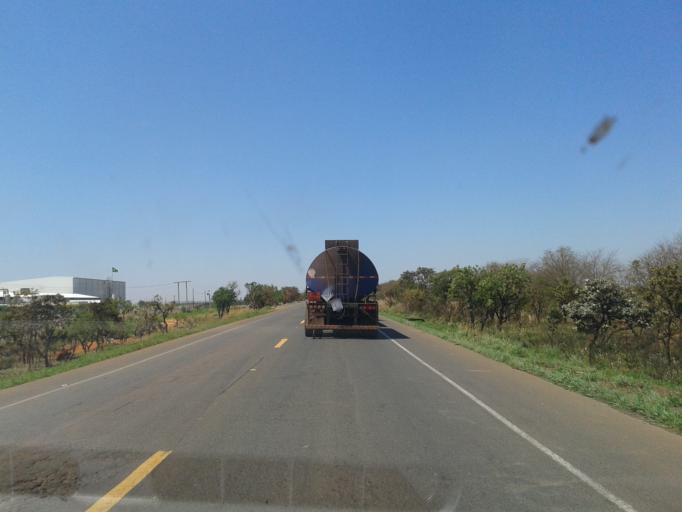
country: BR
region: Minas Gerais
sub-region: Araxa
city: Araxa
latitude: -19.3118
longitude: -47.3902
